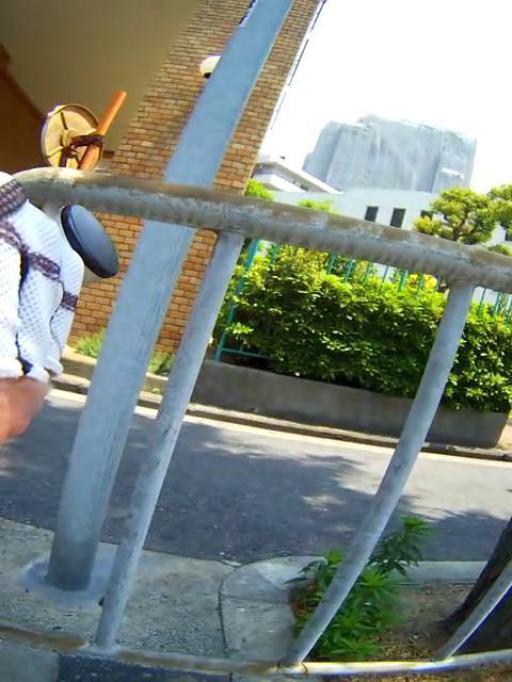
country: JP
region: Osaka
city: Suita
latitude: 34.7782
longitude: 135.4967
